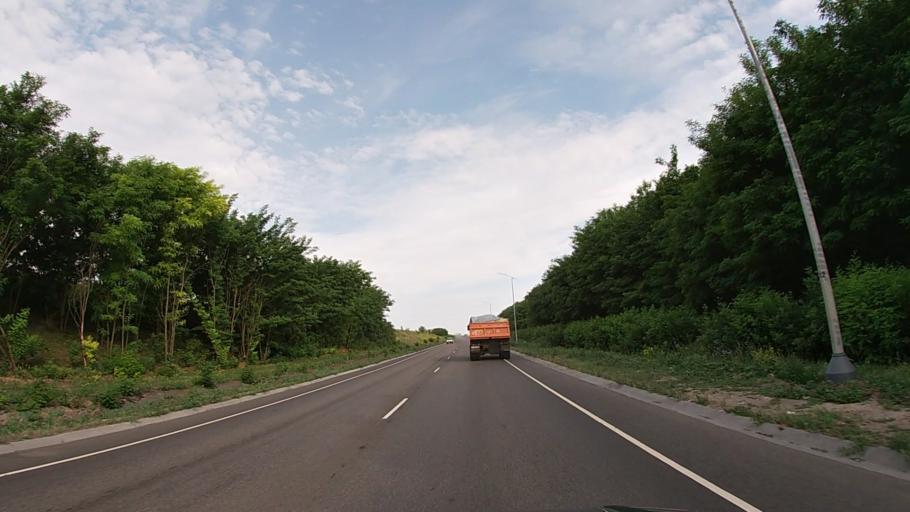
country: RU
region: Belgorod
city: Severnyy
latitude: 50.6690
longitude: 36.4887
